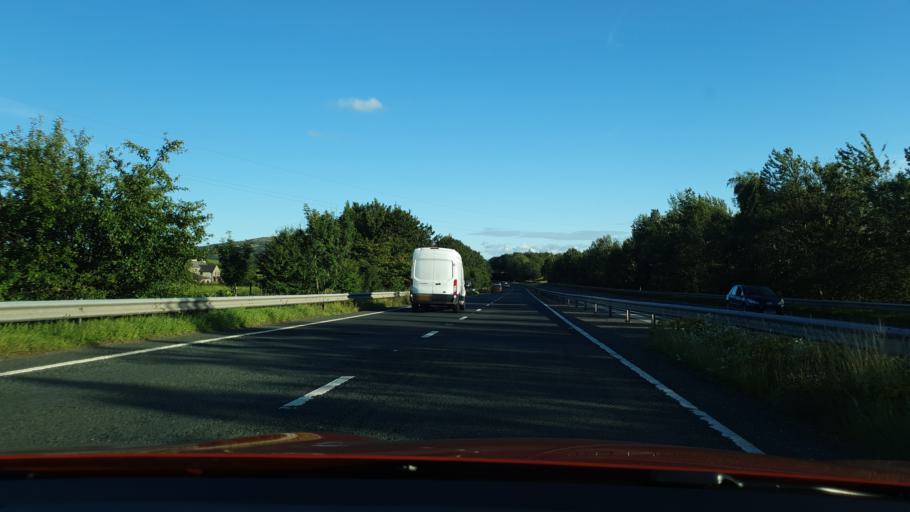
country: GB
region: England
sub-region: Cumbria
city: Milnthorpe
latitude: 54.2476
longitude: -2.7319
